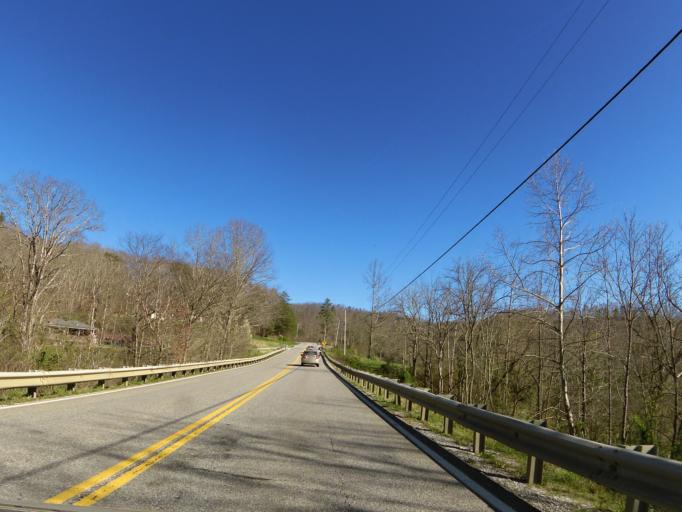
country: US
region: Tennessee
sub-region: Scott County
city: Huntsville
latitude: 36.4344
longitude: -84.4580
